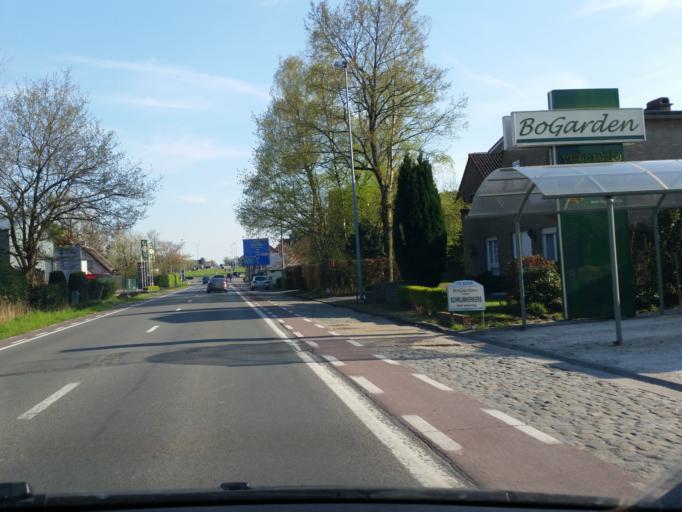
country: BE
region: Flanders
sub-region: Provincie Oost-Vlaanderen
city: Stekene
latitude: 51.2316
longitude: 4.0599
